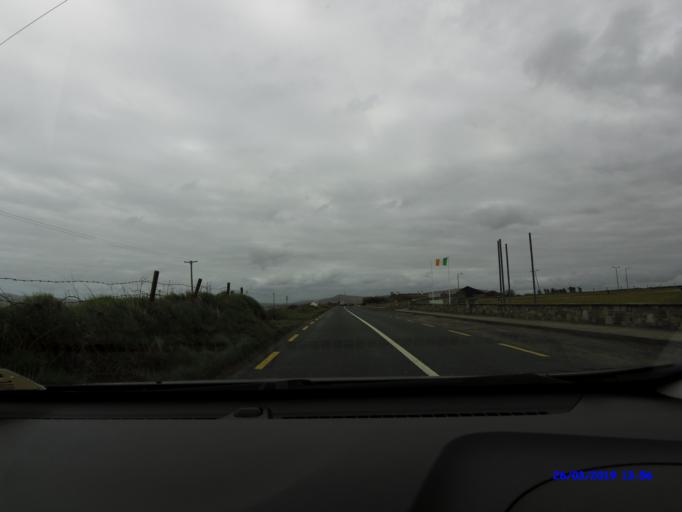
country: IE
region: Connaught
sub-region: Maigh Eo
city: Belmullet
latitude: 54.2092
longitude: -9.9434
